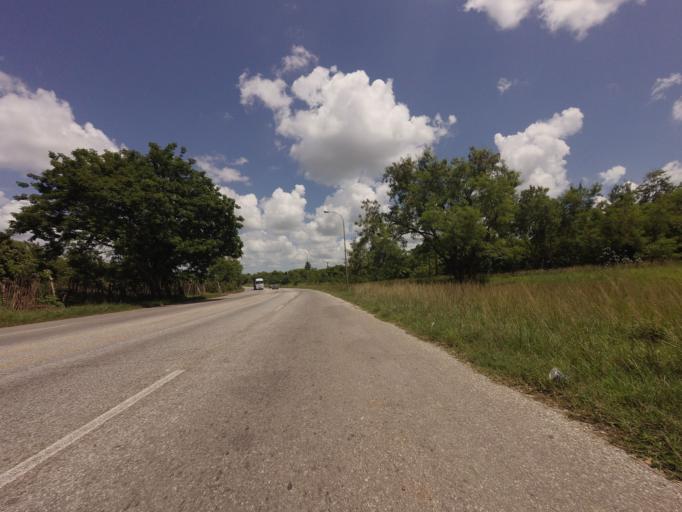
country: CU
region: La Habana
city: Arroyo Naranjo
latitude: 23.0358
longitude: -82.3507
